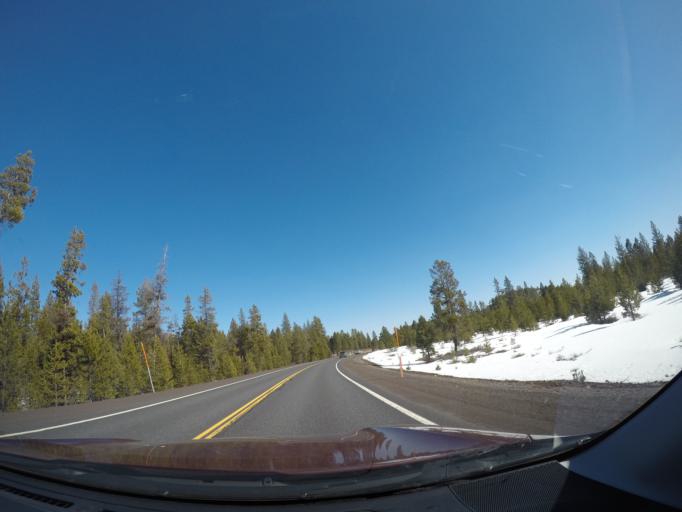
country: US
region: Oregon
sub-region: Deschutes County
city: Three Rivers
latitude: 43.8575
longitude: -121.5165
